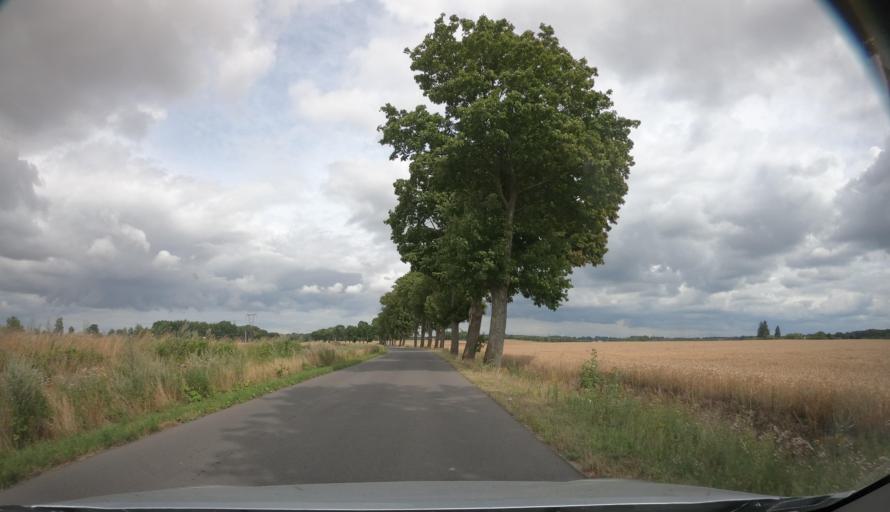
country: PL
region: West Pomeranian Voivodeship
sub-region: Koszalin
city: Koszalin
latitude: 54.1480
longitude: 16.0837
